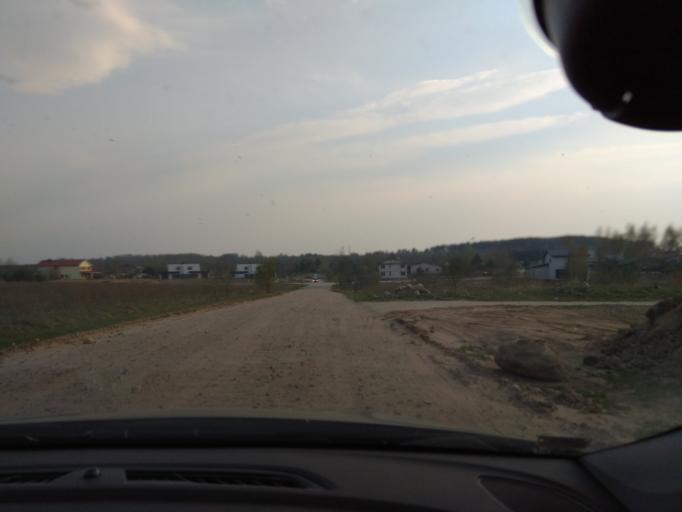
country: LT
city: Baltoji Voke
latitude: 54.5938
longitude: 25.1595
